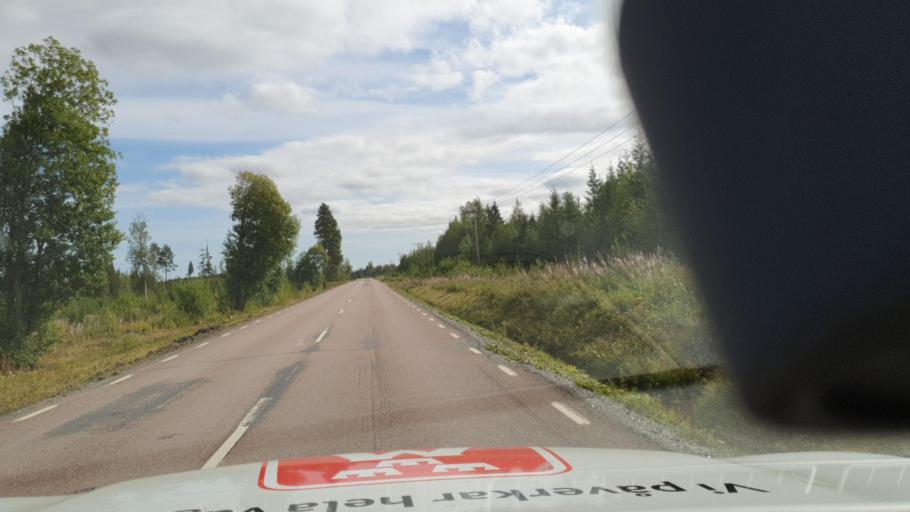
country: SE
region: Jaemtland
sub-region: Stroemsunds Kommun
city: Stroemsund
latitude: 63.8148
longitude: 15.6461
